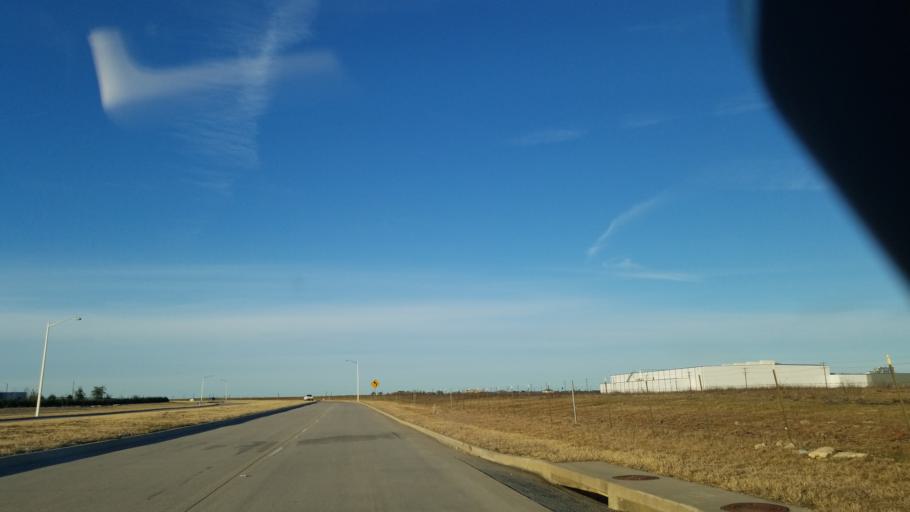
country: US
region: Texas
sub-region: Denton County
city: Denton
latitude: 33.2114
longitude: -97.1844
